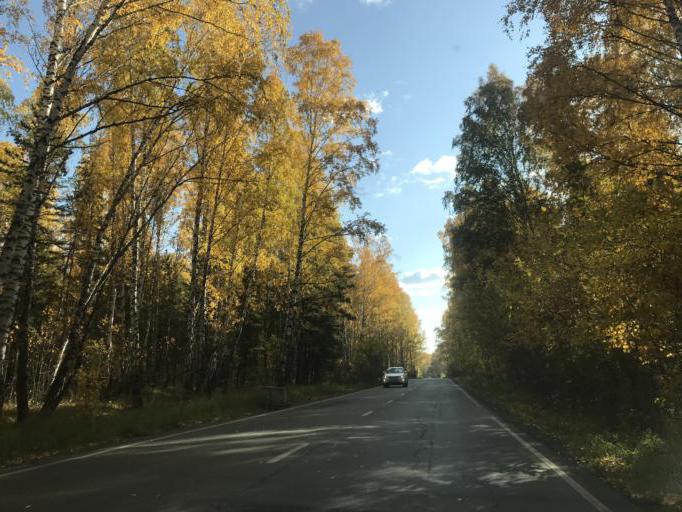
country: RU
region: Chelyabinsk
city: Dolgoderevenskoye
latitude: 55.2675
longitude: 61.3647
